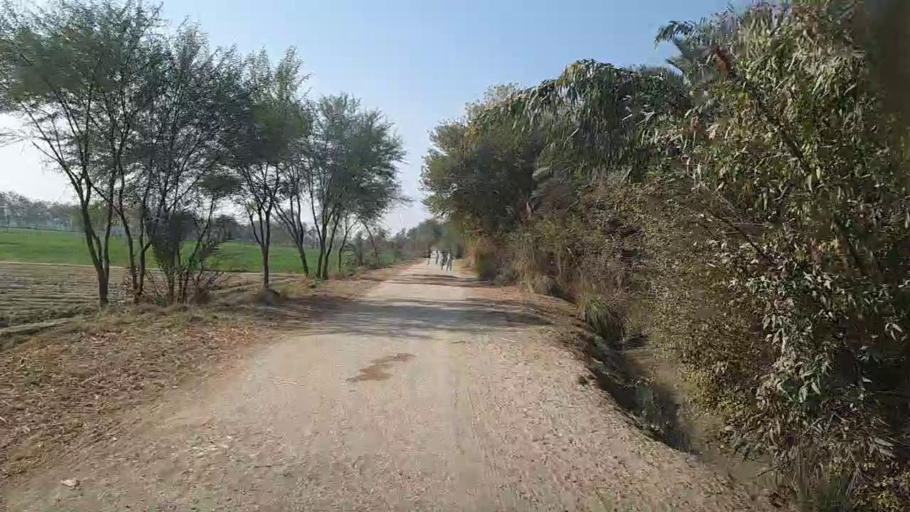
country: PK
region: Sindh
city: Mirpur Mathelo
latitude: 27.9002
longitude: 69.6399
